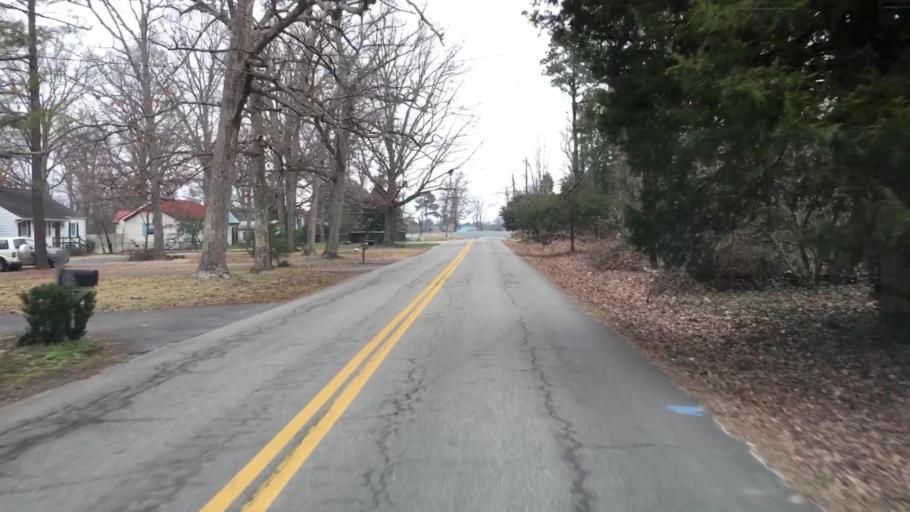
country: US
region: Virginia
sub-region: Chesterfield County
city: Bon Air
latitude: 37.5336
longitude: -77.5626
